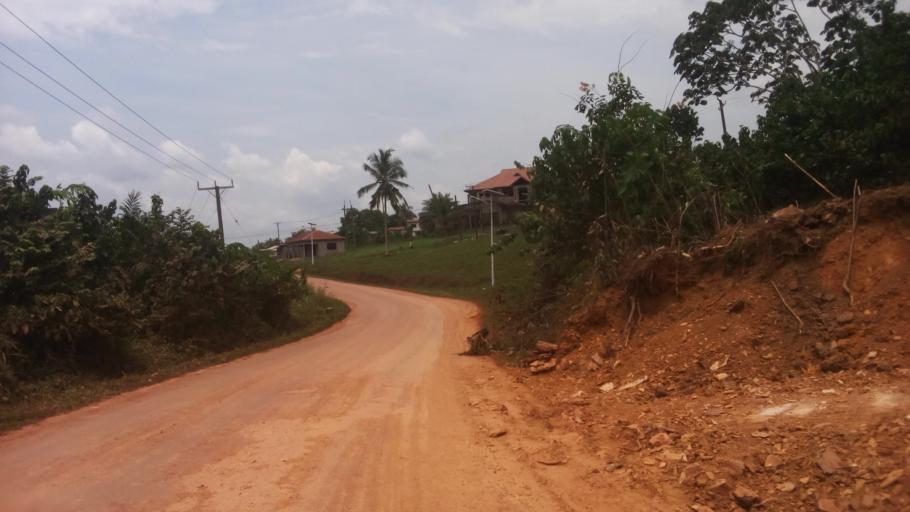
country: GH
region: Western
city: Tarkwa
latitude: 5.3027
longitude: -2.0021
